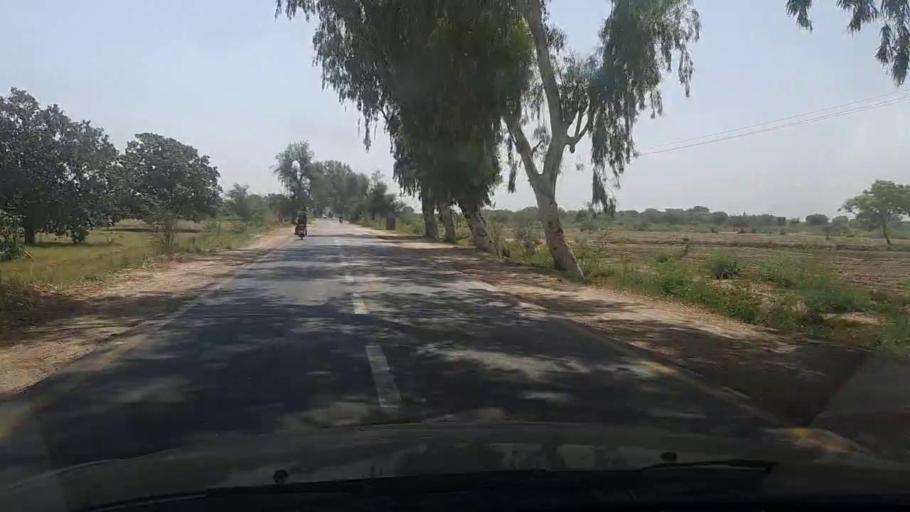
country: PK
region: Sindh
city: Tando Jam
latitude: 25.3228
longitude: 68.5520
